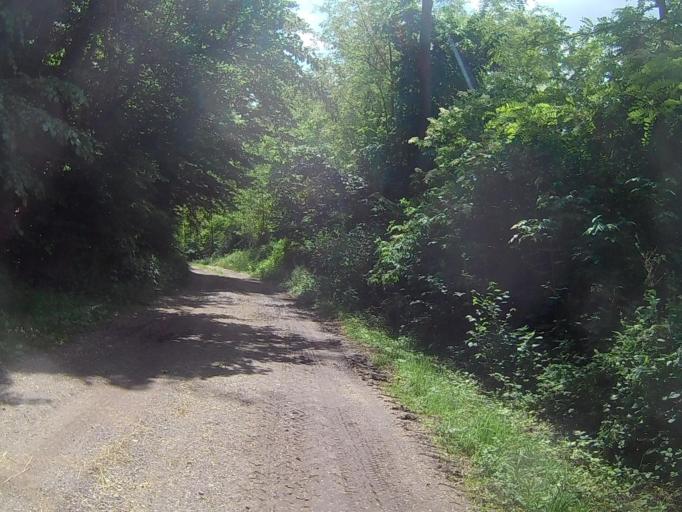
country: SI
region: Miklavz na Dravskem Polju
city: Miklavz na Dravskem Polju
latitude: 46.5144
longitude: 15.7018
